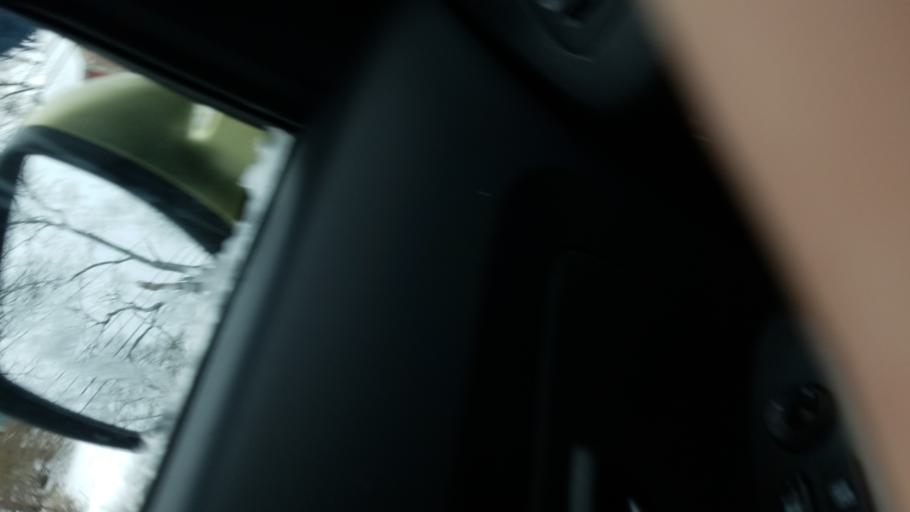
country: US
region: Pennsylvania
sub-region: Jefferson County
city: Punxsutawney
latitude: 40.9506
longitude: -78.9598
